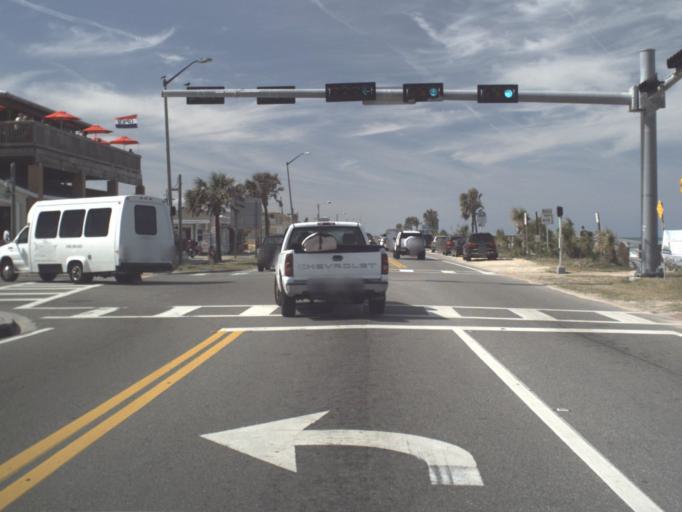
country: US
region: Florida
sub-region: Flagler County
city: Flagler Beach
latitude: 29.4807
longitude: -81.1273
